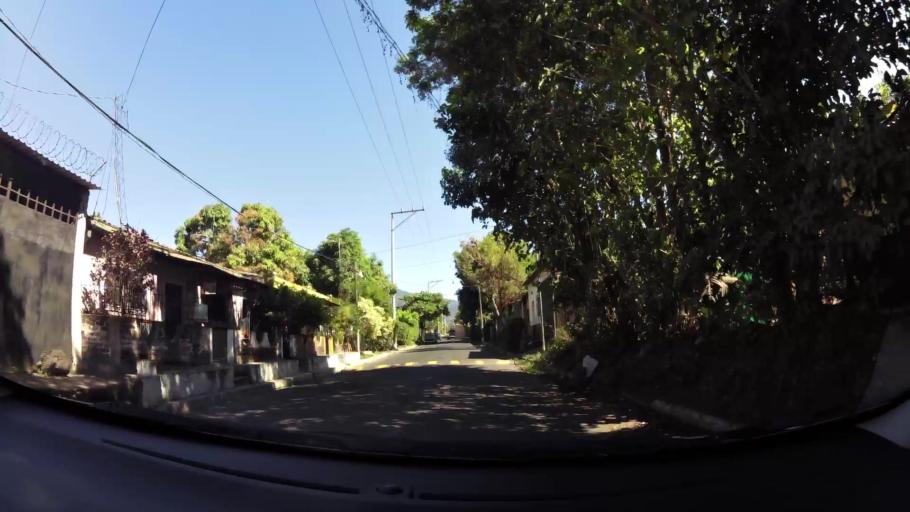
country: SV
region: La Libertad
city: Santa Tecla
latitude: 13.7311
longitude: -89.3699
